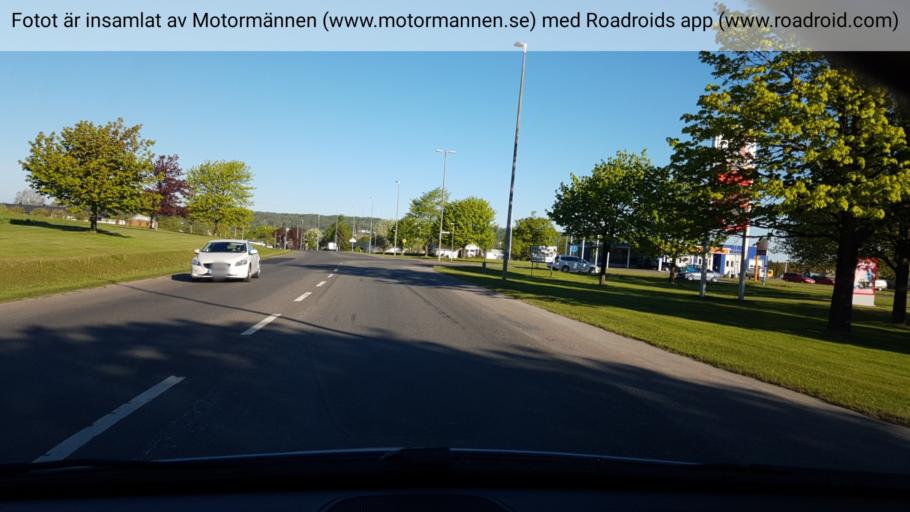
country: SE
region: Vaestra Goetaland
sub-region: Falkopings Kommun
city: Falkoeping
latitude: 58.1699
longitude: 13.5802
